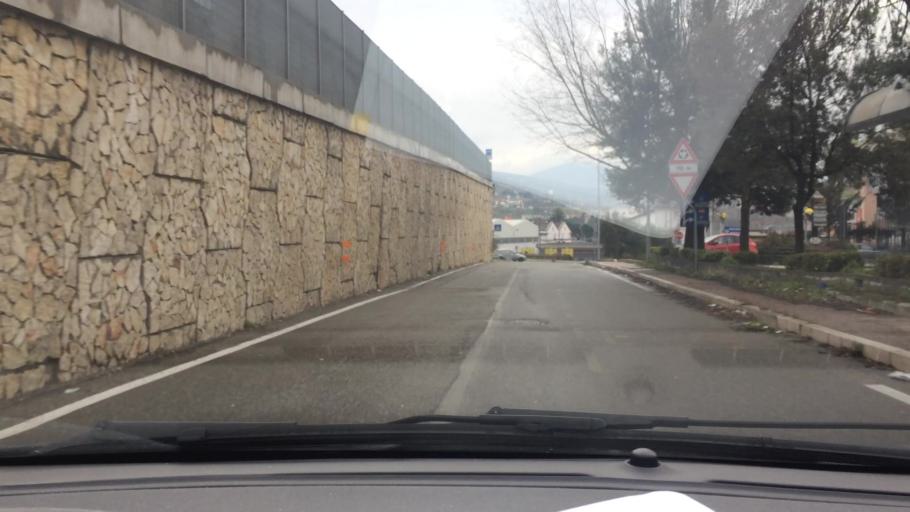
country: IT
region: Basilicate
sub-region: Provincia di Potenza
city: Potenza
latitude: 40.6301
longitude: 15.7966
